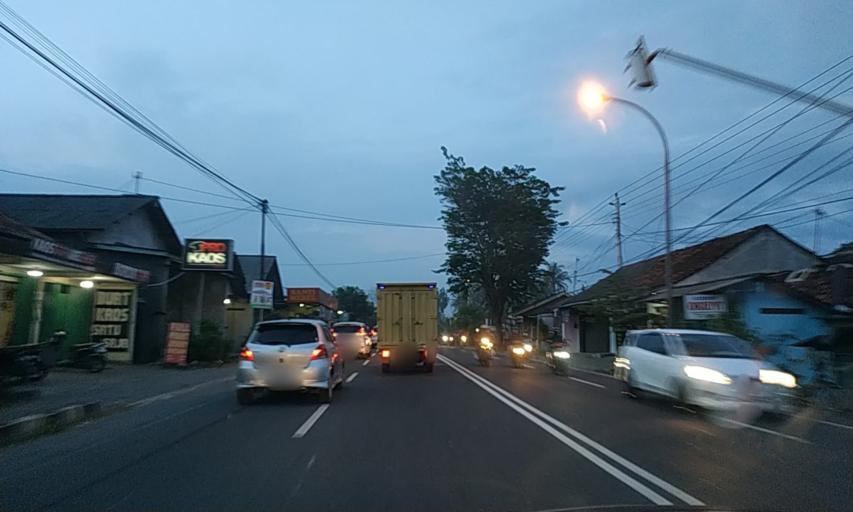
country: ID
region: Daerah Istimewa Yogyakarta
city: Godean
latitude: -7.8342
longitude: 110.2204
